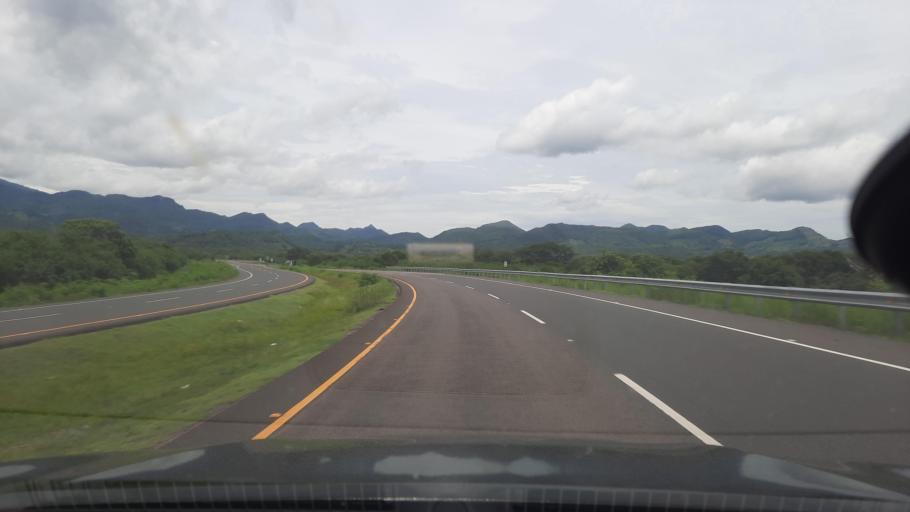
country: HN
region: Valle
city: Aramecina
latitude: 13.7293
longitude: -87.7168
